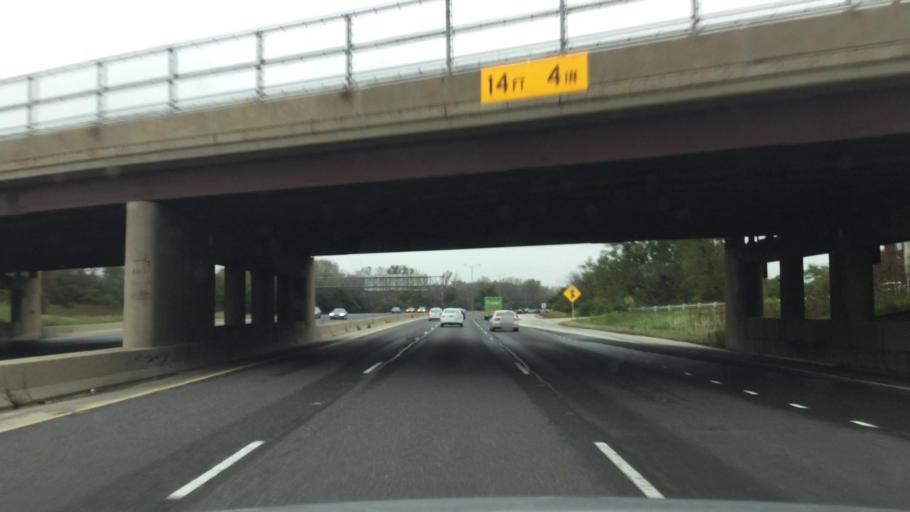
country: US
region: Illinois
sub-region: Cook County
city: Glencoe
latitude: 42.1381
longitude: -87.7885
